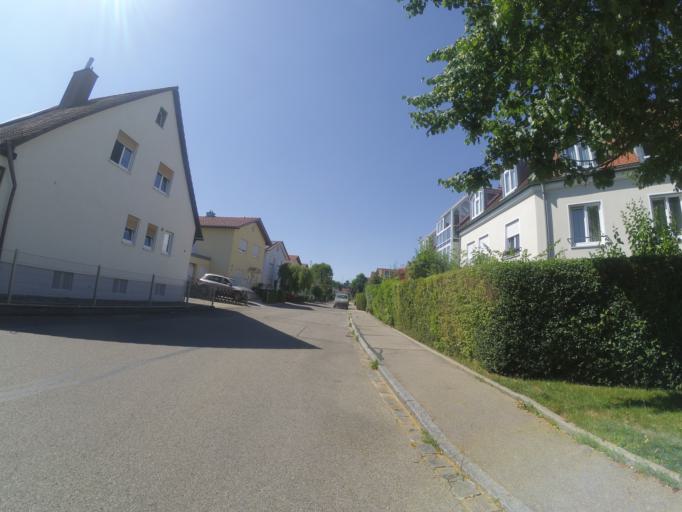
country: DE
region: Bavaria
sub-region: Swabia
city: Memmingen
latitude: 47.9836
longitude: 10.1918
